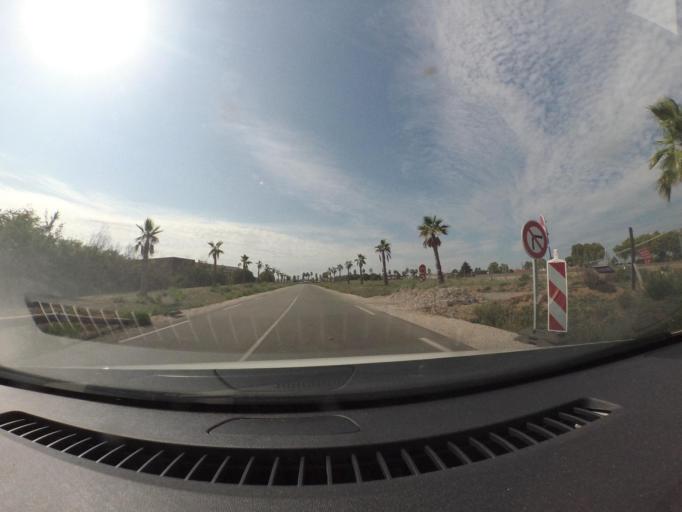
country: FR
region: Languedoc-Roussillon
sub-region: Departement de l'Herault
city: Baillargues
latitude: 43.6535
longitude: 4.0042
